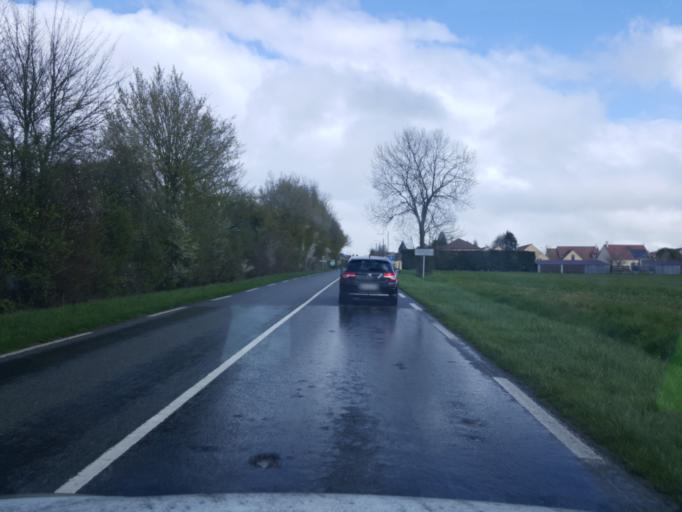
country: FR
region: Picardie
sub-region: Departement de l'Oise
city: Auneuil
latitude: 49.3518
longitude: 1.9375
